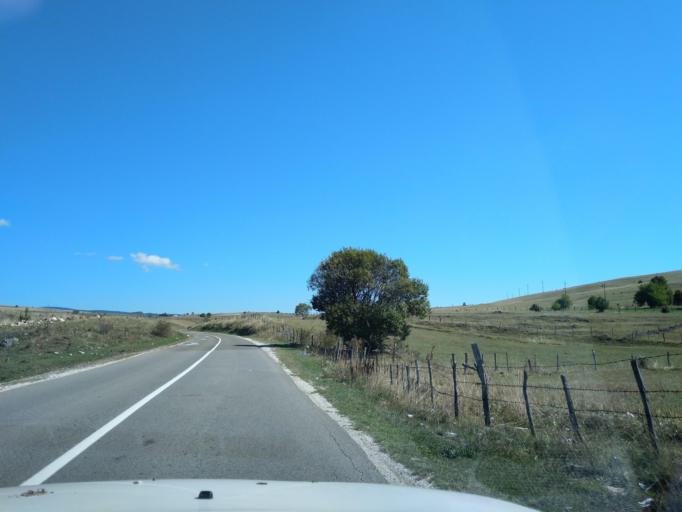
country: RS
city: Sokolovica
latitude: 43.2738
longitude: 20.2035
